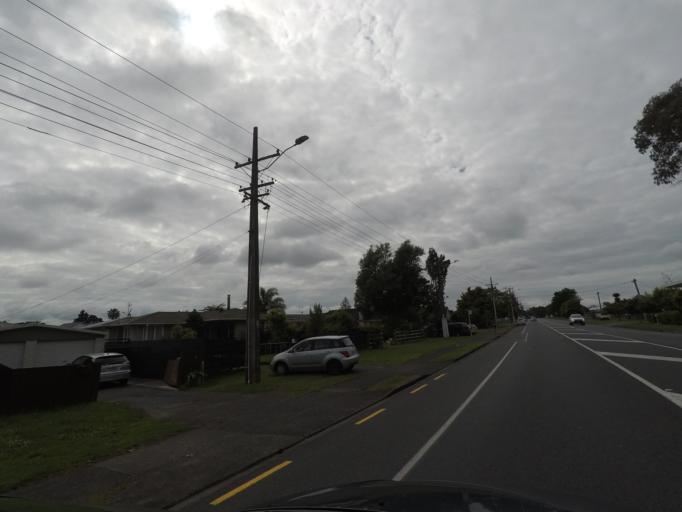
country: NZ
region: Auckland
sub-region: Auckland
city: Rosebank
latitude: -36.8694
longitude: 174.6180
